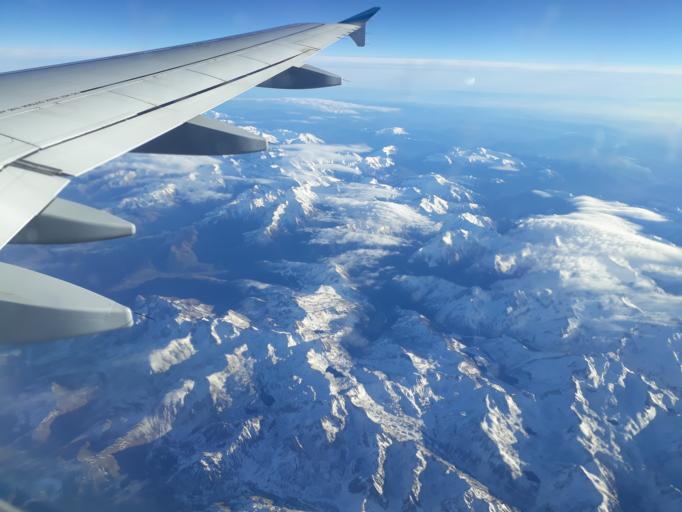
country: FR
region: Midi-Pyrenees
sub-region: Departement des Hautes-Pyrenees
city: Campan
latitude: 42.9756
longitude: 0.0937
